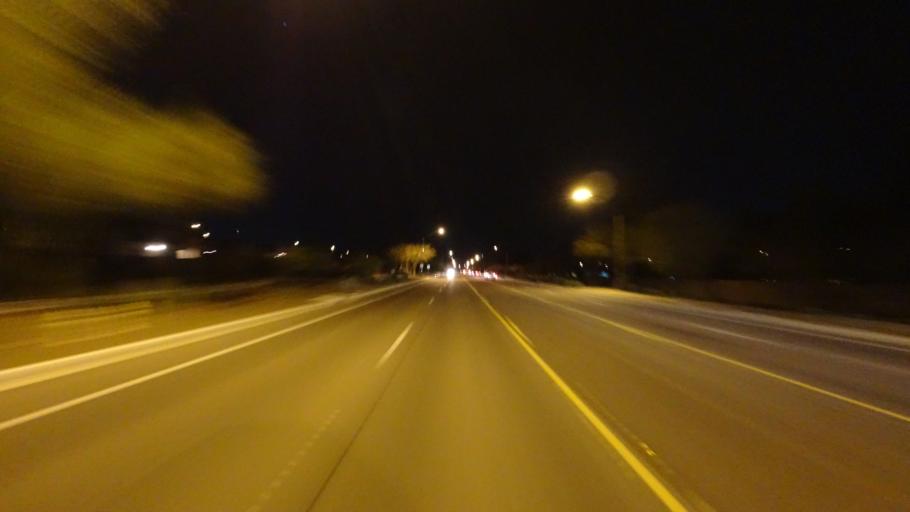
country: US
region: Arizona
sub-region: Maricopa County
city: Gilbert
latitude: 33.3045
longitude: -111.7728
